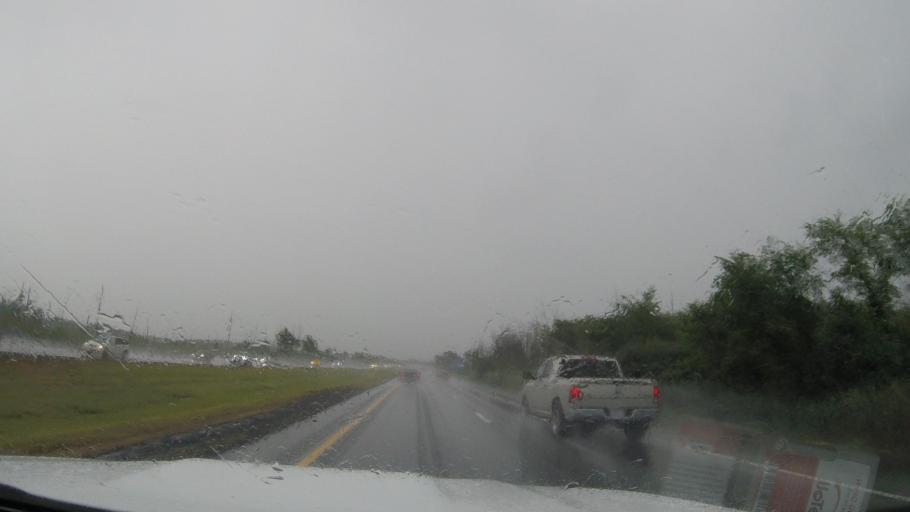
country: US
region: New York
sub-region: Seneca County
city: Waterloo
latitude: 42.9620
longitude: -76.8910
